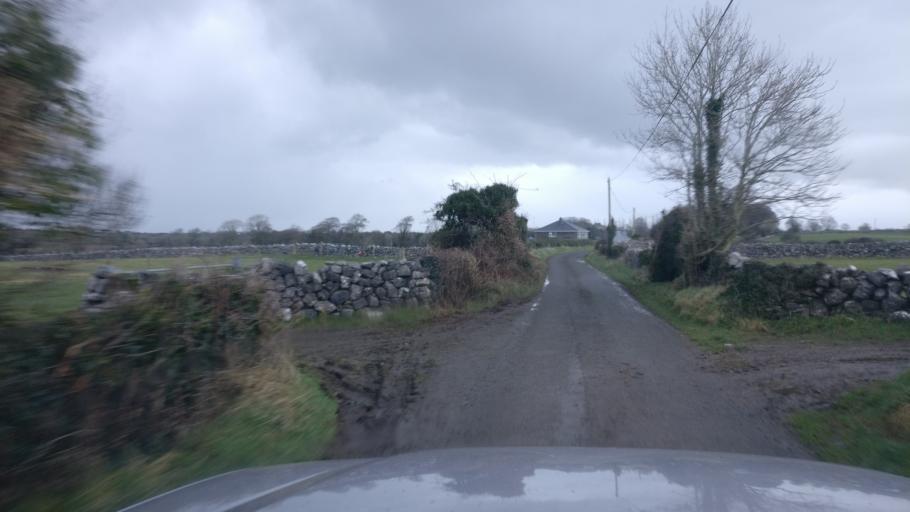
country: IE
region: Connaught
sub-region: County Galway
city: Loughrea
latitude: 53.1819
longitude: -8.6773
